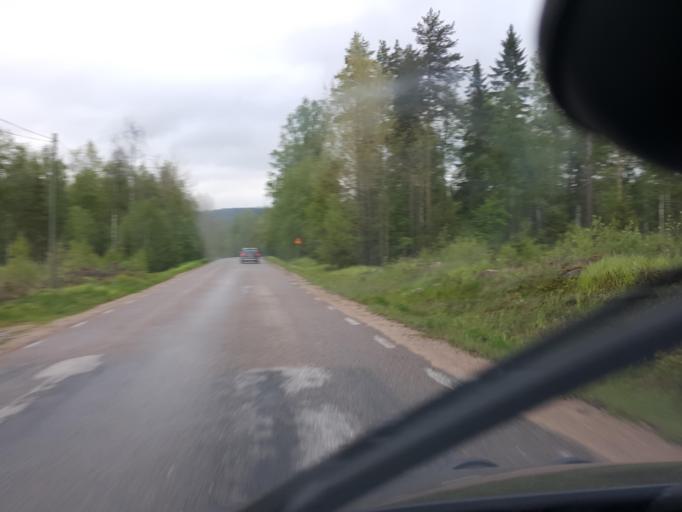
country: SE
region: Gaevleborg
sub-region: Ljusdals Kommun
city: Jaervsoe
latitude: 61.7870
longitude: 16.2175
